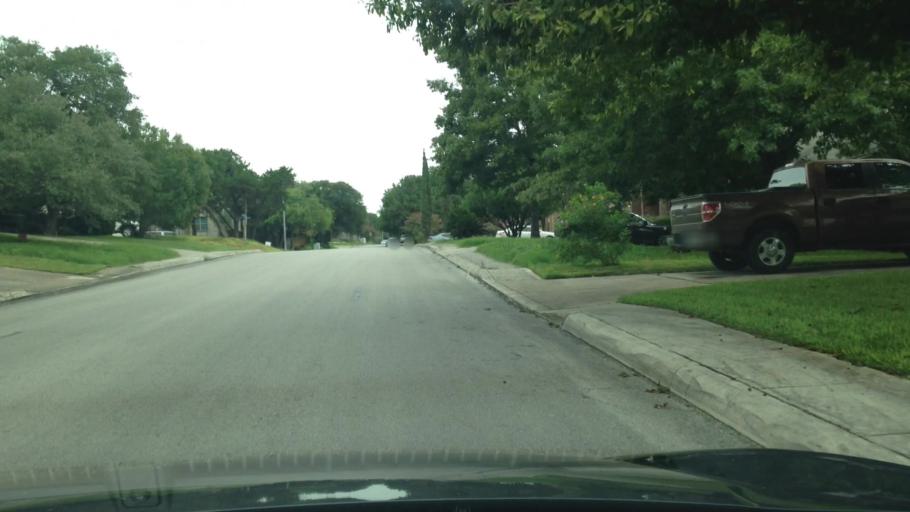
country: US
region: Texas
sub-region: Bexar County
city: Live Oak
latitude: 29.5885
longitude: -98.4026
